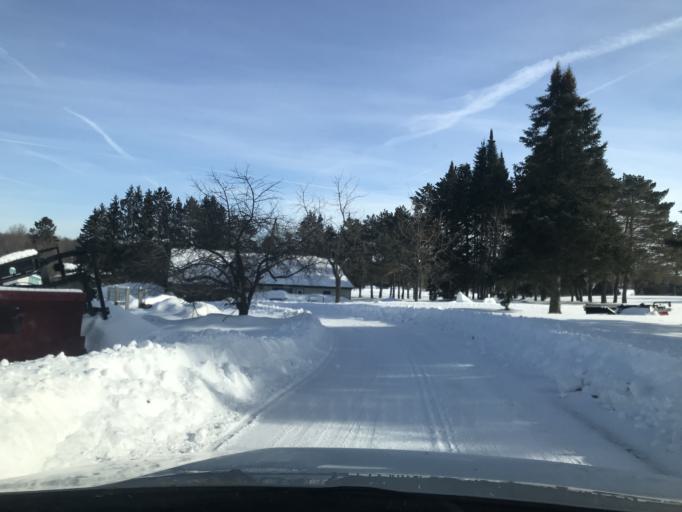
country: US
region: Wisconsin
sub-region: Menominee County
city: Legend Lake
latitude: 45.2979
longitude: -88.4979
